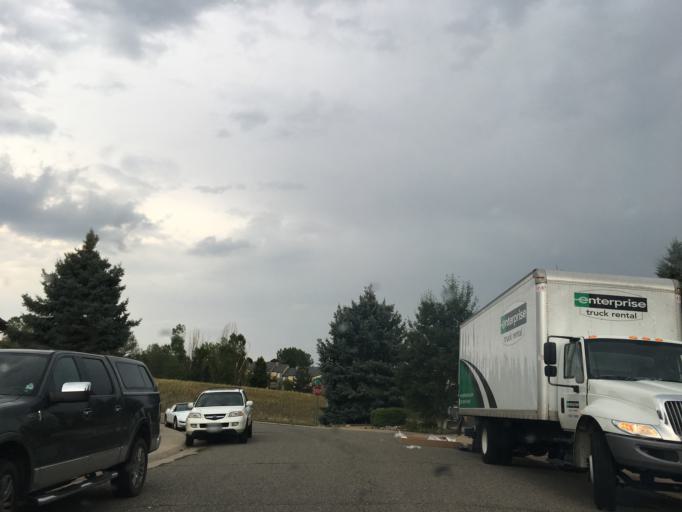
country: US
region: Colorado
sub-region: Arapahoe County
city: Sheridan
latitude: 39.6589
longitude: -105.0338
